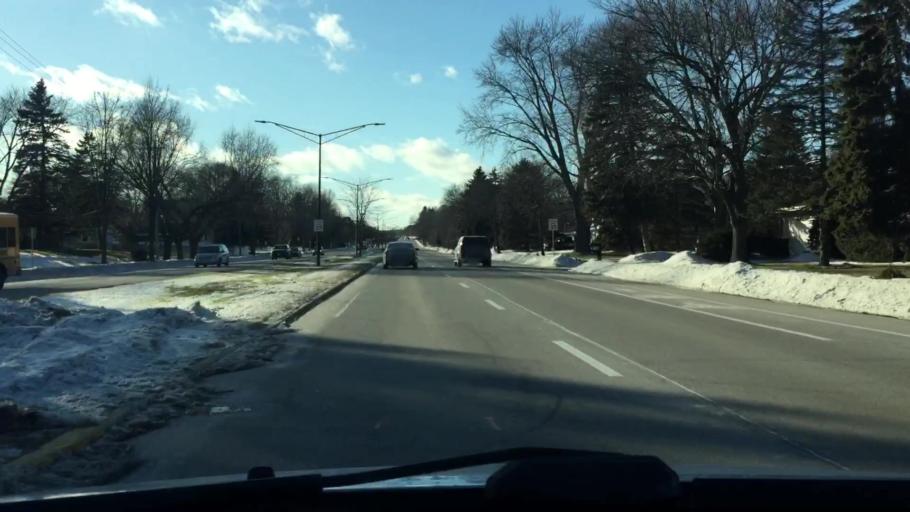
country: US
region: Wisconsin
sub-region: Waukesha County
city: New Berlin
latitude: 42.9882
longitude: -88.0600
